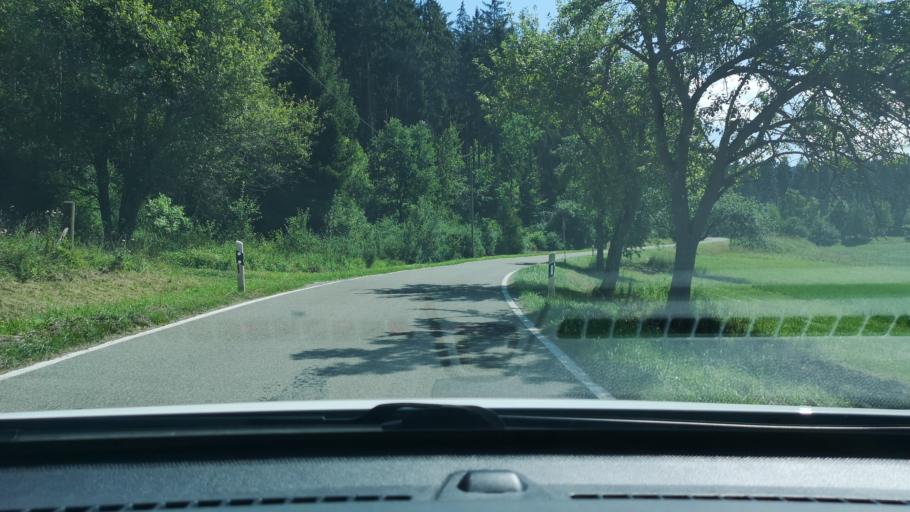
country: DE
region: Baden-Wuerttemberg
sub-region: Freiburg Region
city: Muhlheim am Bach
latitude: 48.3598
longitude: 8.7141
